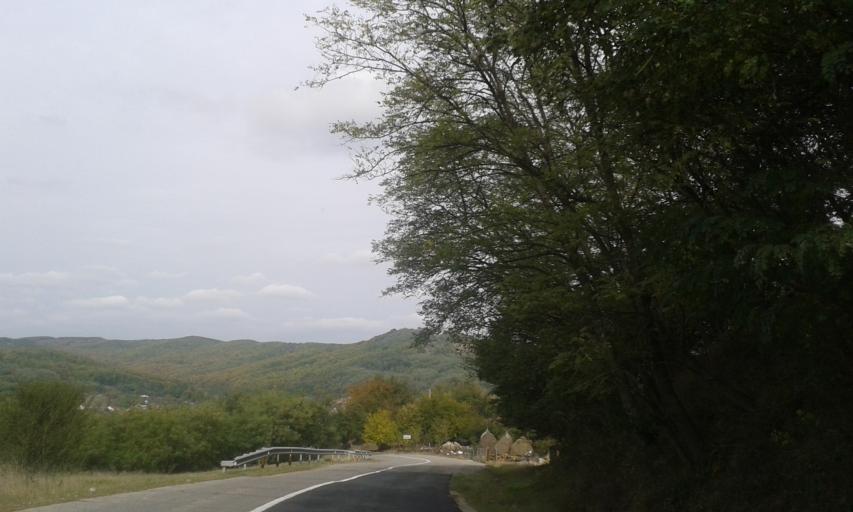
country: RO
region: Gorj
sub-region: Comuna Stejari
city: Piscoiu
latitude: 44.9135
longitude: 23.7708
